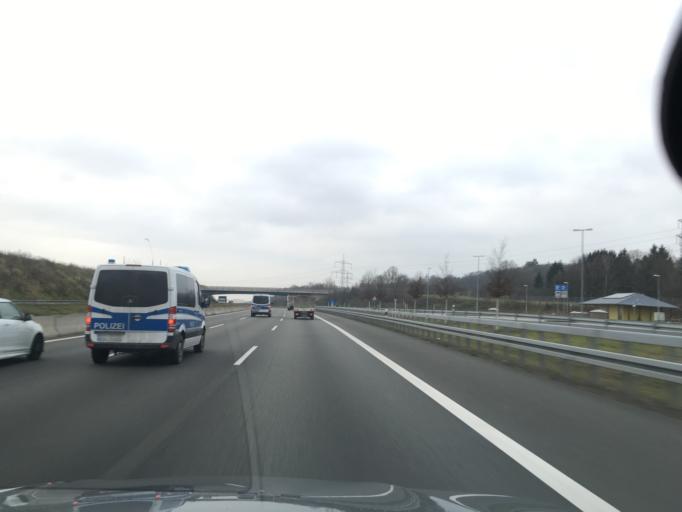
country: DE
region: Bavaria
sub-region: Regierungsbezirk Unterfranken
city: Glattbach
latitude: 49.9952
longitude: 9.1200
